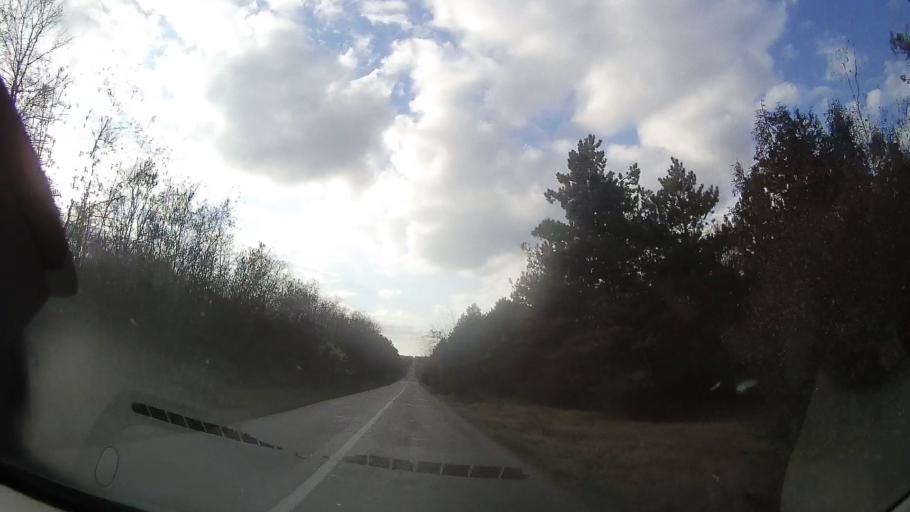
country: RO
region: Constanta
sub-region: Comuna Negru Voda
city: Negru Voda
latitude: 43.8193
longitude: 28.2723
